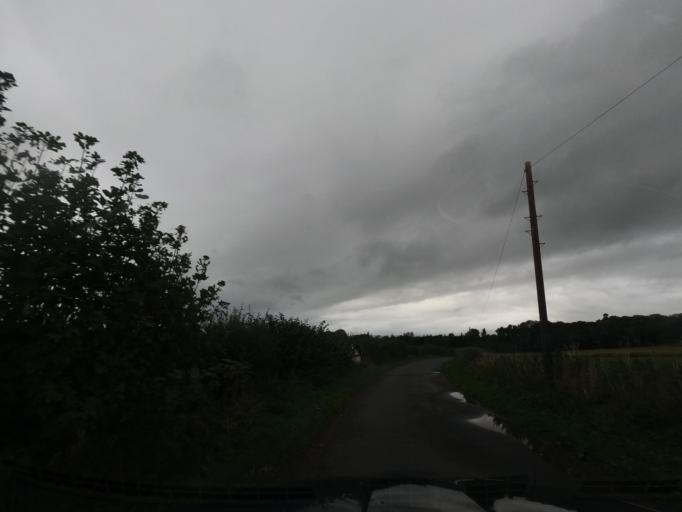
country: GB
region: England
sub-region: Northumberland
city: Ford
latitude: 55.6269
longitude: -2.0875
